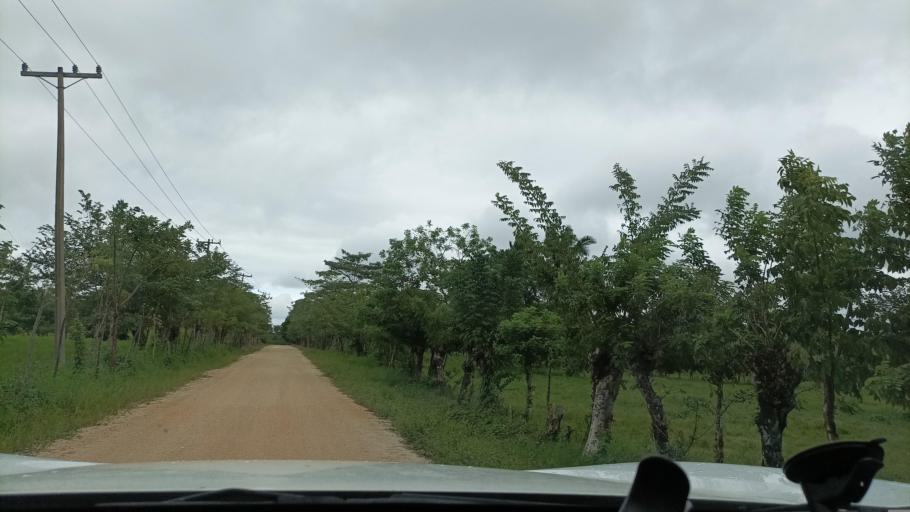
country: MX
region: Veracruz
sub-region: Moloacan
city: Cuichapa
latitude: 17.8148
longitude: -94.3552
